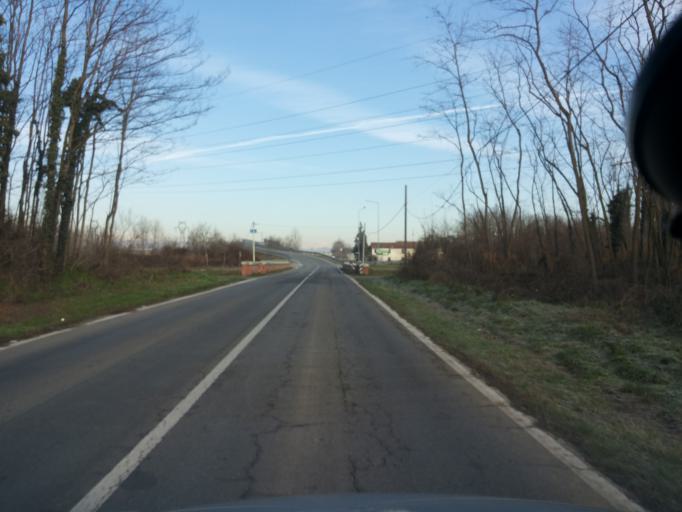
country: IT
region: Piedmont
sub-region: Provincia di Vercelli
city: Greggio
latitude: 45.4577
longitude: 8.3855
